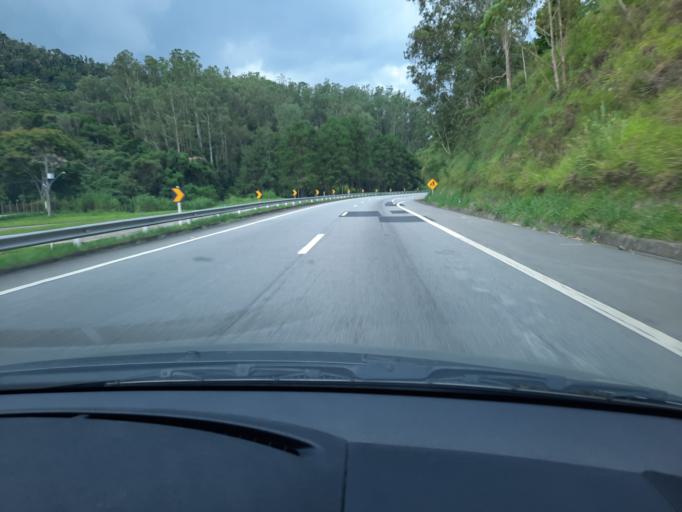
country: BR
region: Rio de Janeiro
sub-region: Petropolis
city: Petropolis
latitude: -22.4358
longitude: -43.1746
